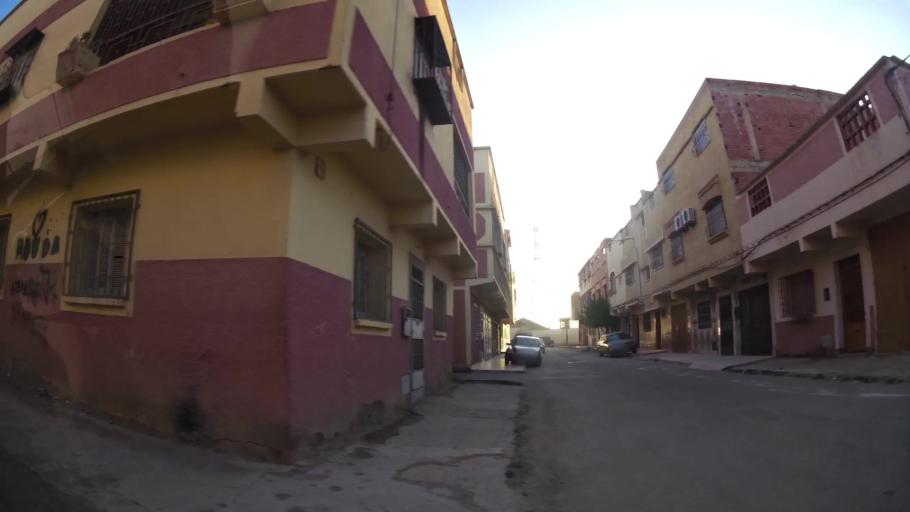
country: MA
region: Oriental
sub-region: Oujda-Angad
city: Oujda
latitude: 34.7070
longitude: -1.9145
